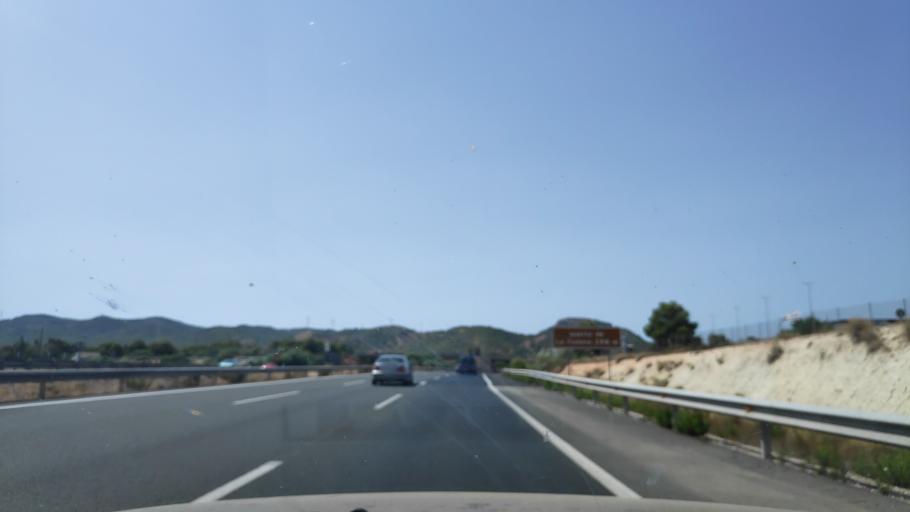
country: ES
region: Murcia
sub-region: Murcia
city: Murcia
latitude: 37.8837
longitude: -1.1361
